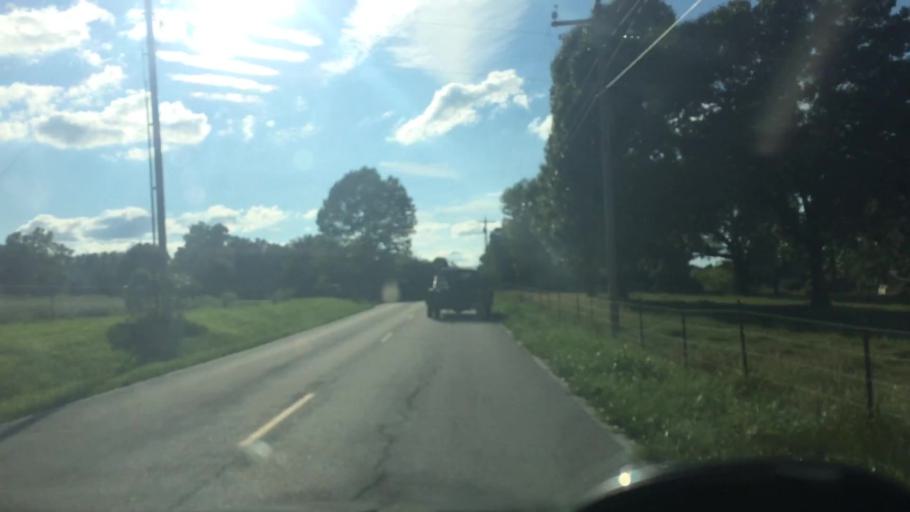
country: US
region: Missouri
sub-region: Greene County
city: Strafford
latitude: 37.2846
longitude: -93.0831
